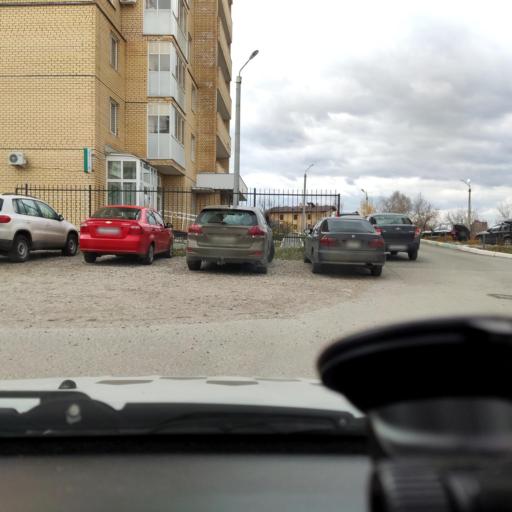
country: RU
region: Perm
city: Perm
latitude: 58.0260
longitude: 56.2877
